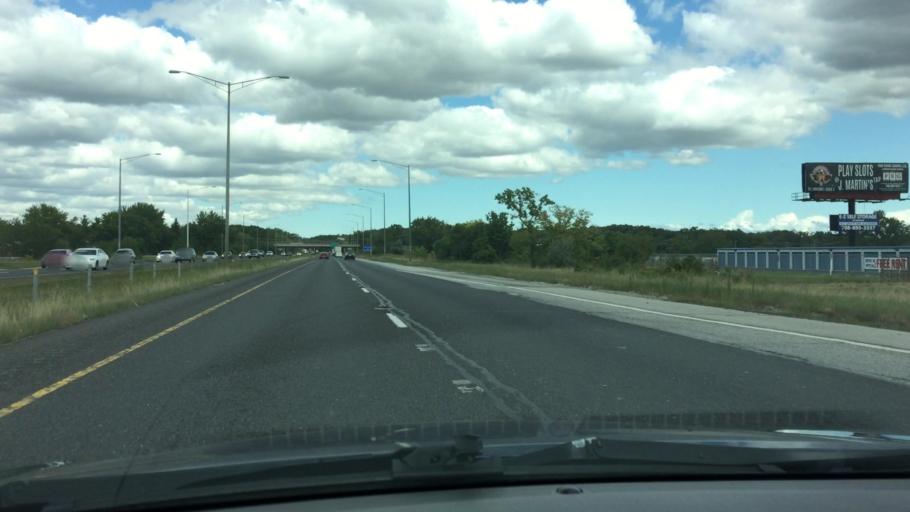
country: US
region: Illinois
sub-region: Cook County
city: Glenwood
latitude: 41.5378
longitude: -87.5824
